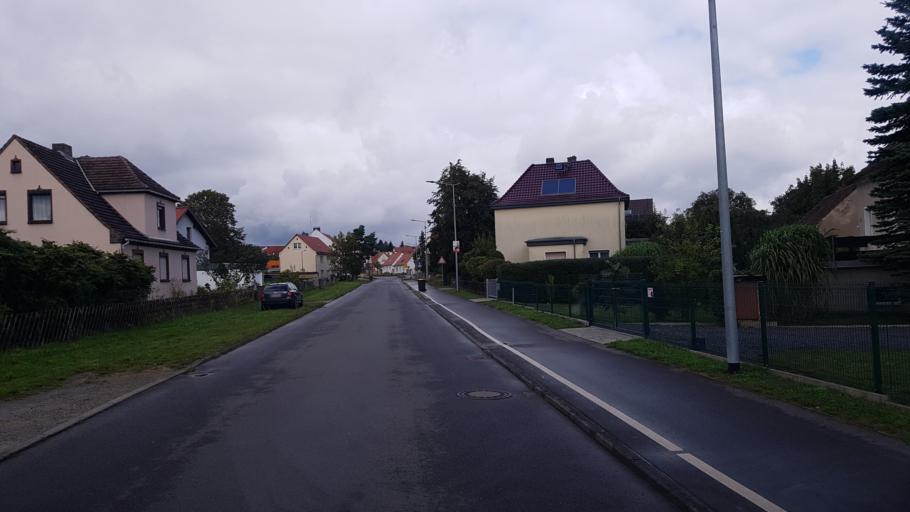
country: DE
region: Brandenburg
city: Lauchhammer
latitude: 51.4912
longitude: 13.7656
